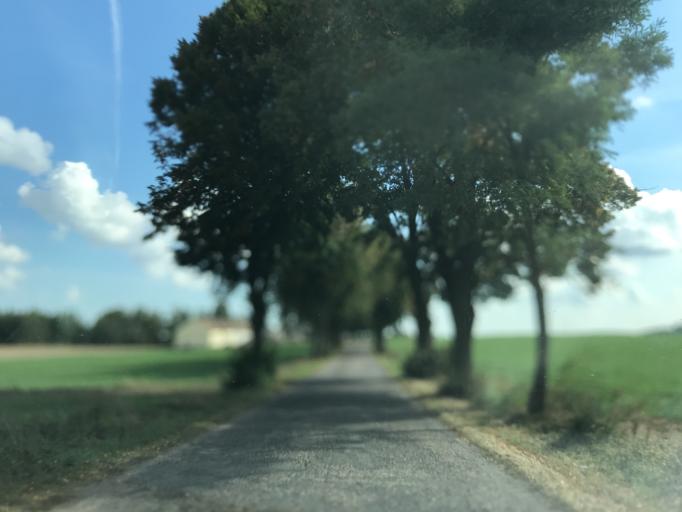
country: PL
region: Kujawsko-Pomorskie
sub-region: Powiat brodnicki
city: Brzozie
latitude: 53.3508
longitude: 19.6485
